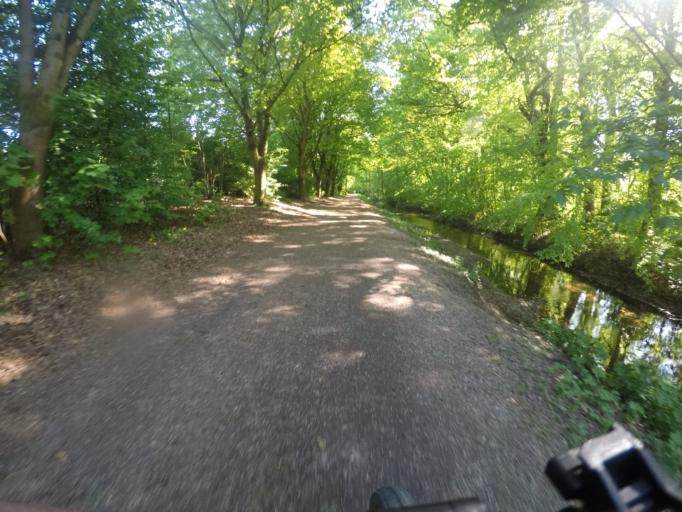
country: DE
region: Hamburg
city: Farmsen-Berne
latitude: 53.6072
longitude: 10.1236
